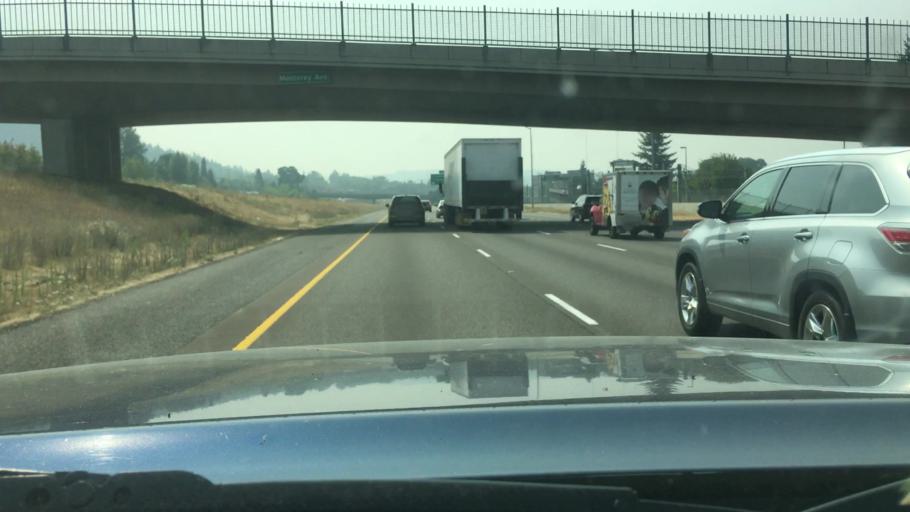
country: US
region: Oregon
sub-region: Clackamas County
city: Clackamas
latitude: 45.4388
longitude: -122.5683
